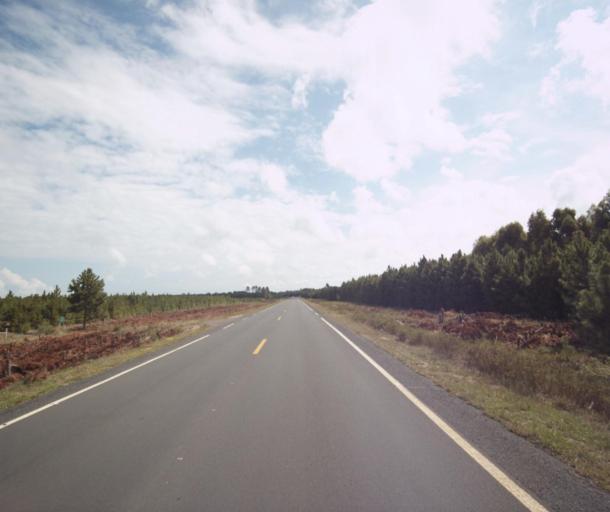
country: BR
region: Rio Grande do Sul
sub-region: Sao Lourenco Do Sul
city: Sao Lourenco do Sul
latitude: -31.4609
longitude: -51.2274
